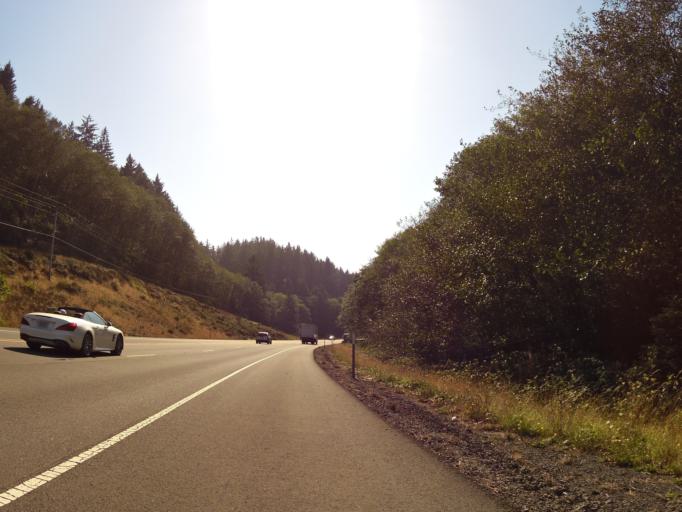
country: US
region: Oregon
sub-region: Tillamook County
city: Pacific City
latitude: 45.1508
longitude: -123.9570
